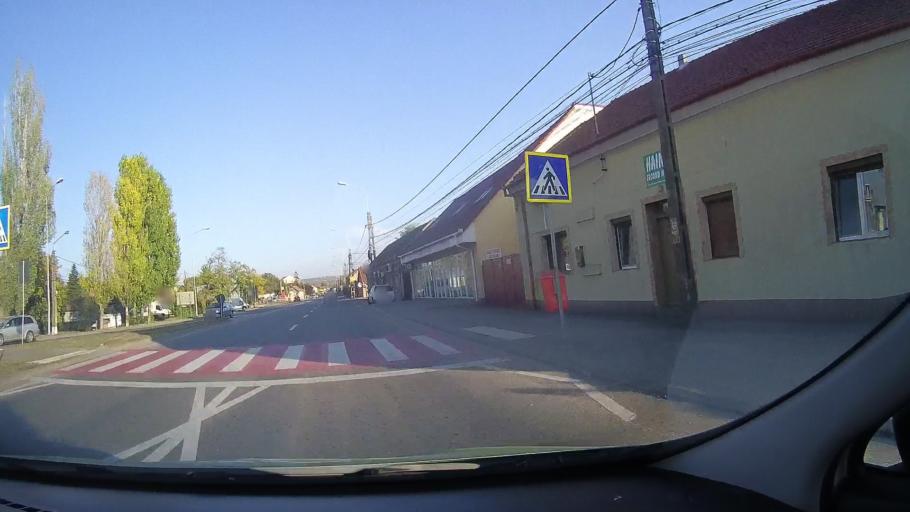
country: RO
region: Bihor
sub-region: Comuna Biharea
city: Biharea
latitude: 47.1030
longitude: 21.8943
